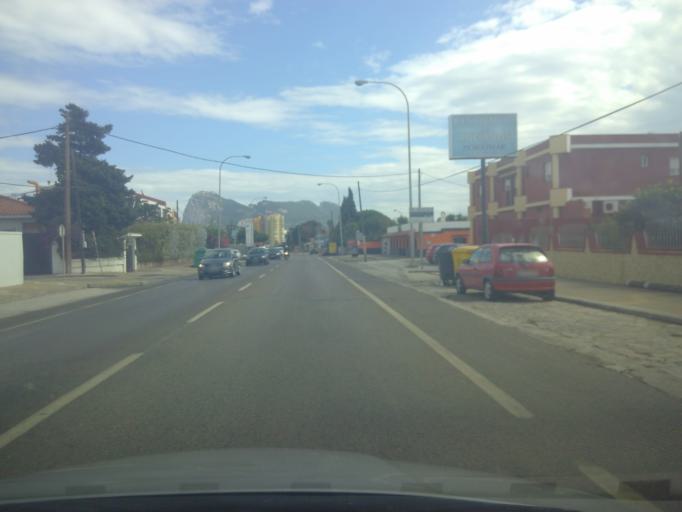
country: ES
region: Andalusia
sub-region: Provincia de Cadiz
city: La Linea de la Concepcion
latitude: 36.1749
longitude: -5.3739
